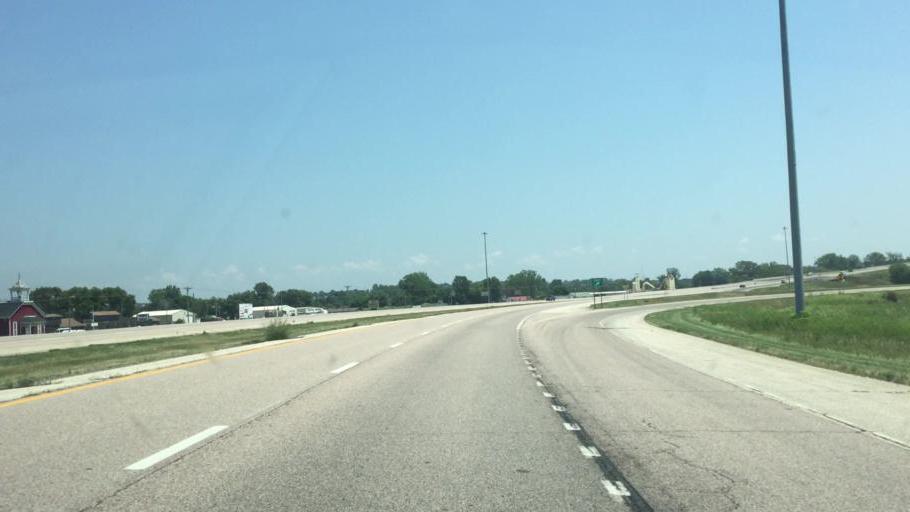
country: US
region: Kansas
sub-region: Doniphan County
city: Elwood
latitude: 39.7487
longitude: -94.8726
